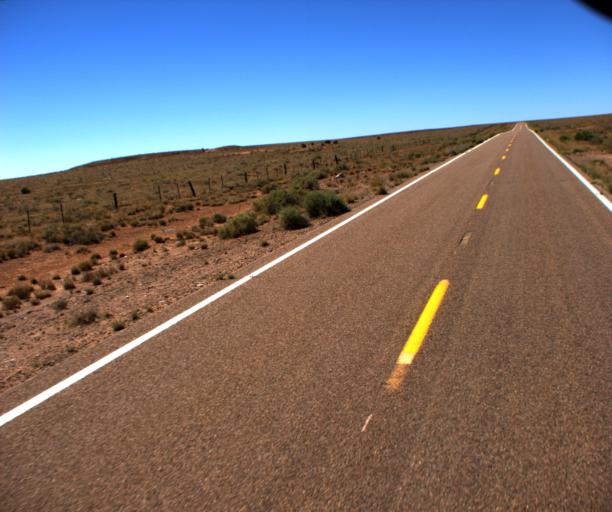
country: US
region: Arizona
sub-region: Navajo County
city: Winslow
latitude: 34.9264
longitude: -110.6378
